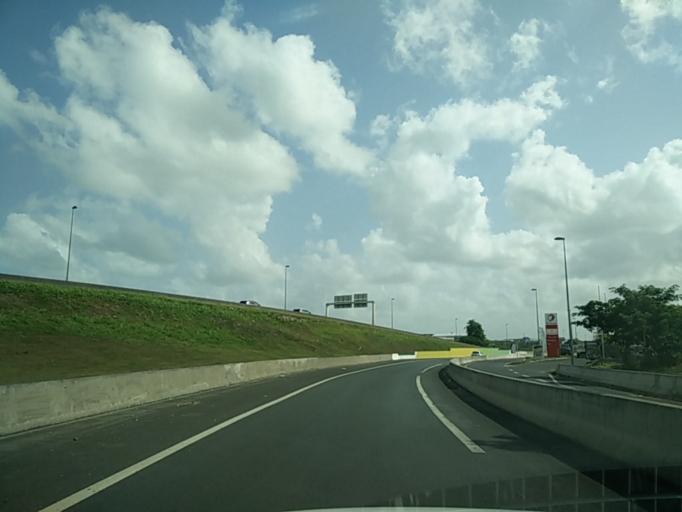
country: GP
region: Guadeloupe
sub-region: Guadeloupe
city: Les Abymes
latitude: 16.2694
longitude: -61.5120
